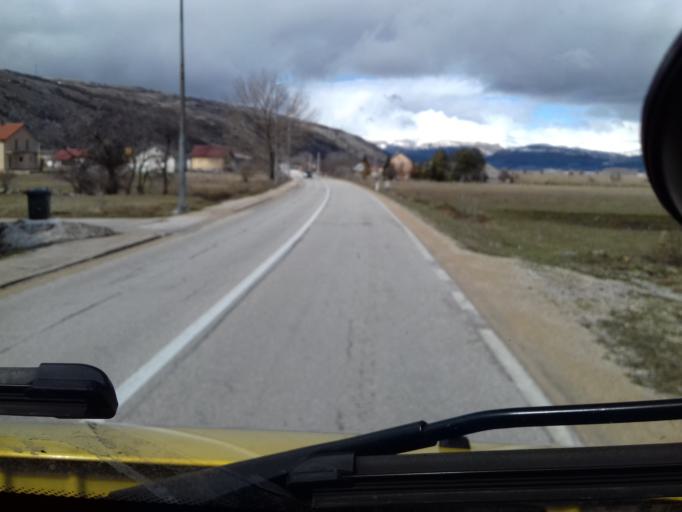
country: BA
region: Federation of Bosnia and Herzegovina
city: Tomislavgrad
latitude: 43.6498
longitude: 17.2258
